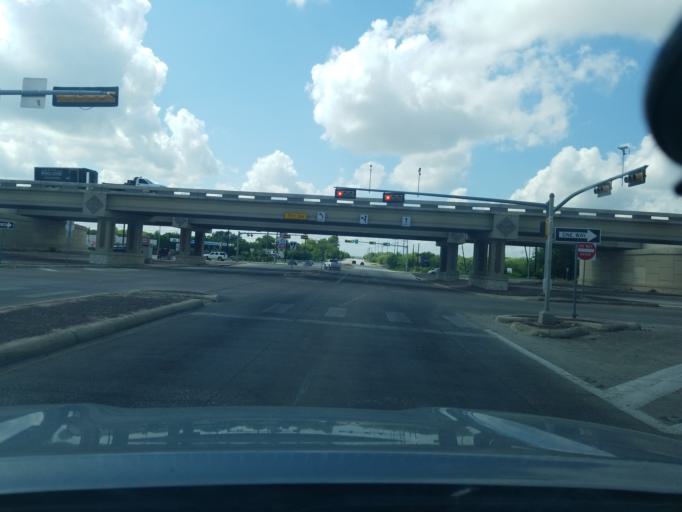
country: US
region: Texas
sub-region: Bexar County
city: Lackland Air Force Base
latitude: 29.3207
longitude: -98.5327
